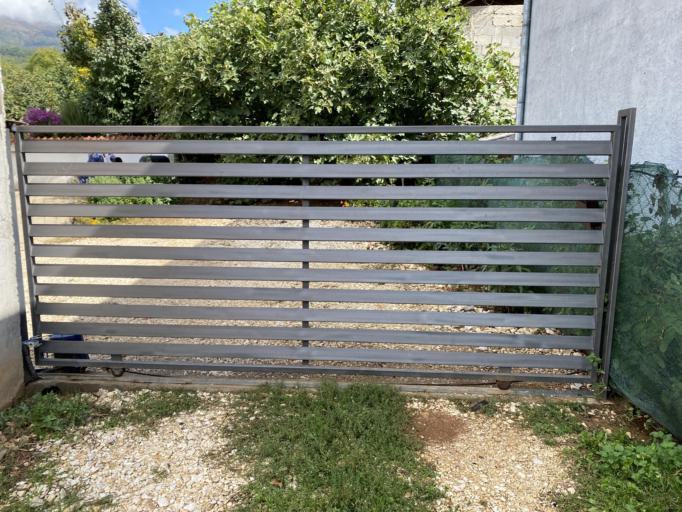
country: MK
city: Radishani
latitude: 42.1044
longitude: 21.4559
